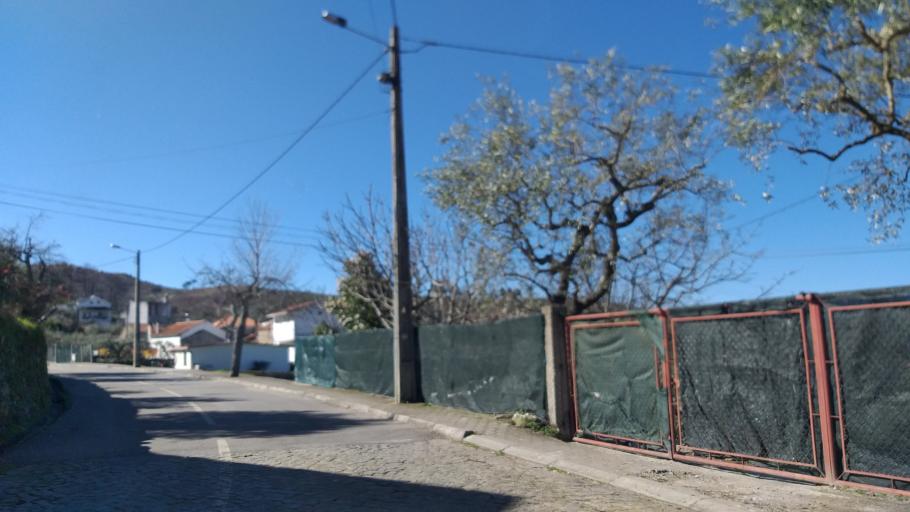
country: PT
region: Guarda
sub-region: Manteigas
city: Manteigas
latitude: 40.4656
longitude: -7.6056
